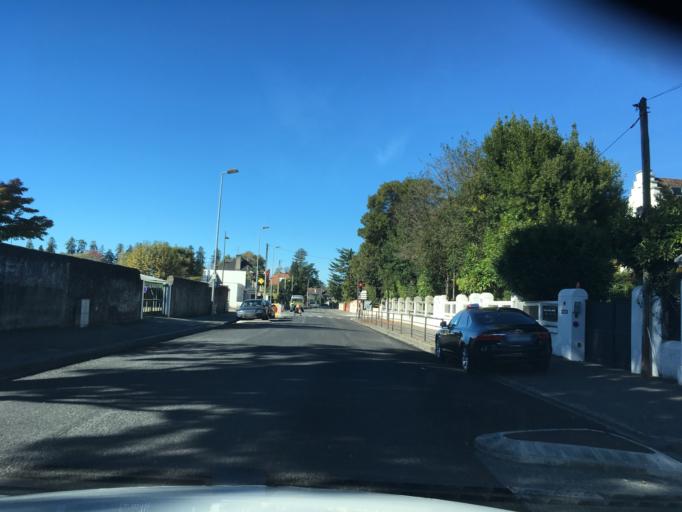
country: FR
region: Aquitaine
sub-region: Departement des Pyrenees-Atlantiques
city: Bizanos
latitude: 43.2988
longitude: -0.3510
